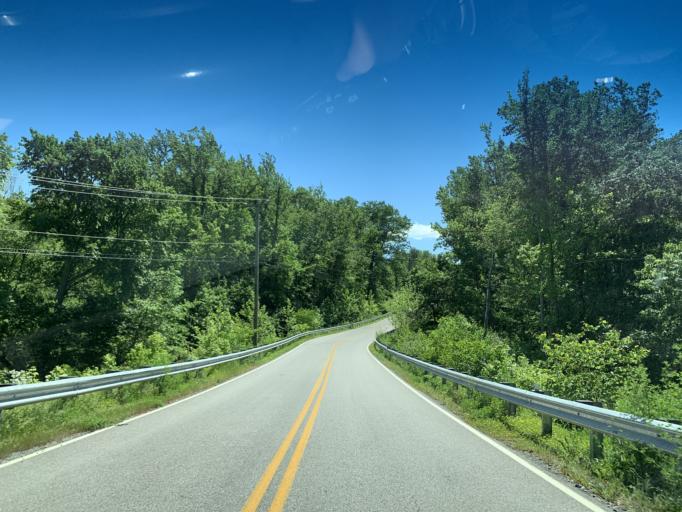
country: US
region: Maryland
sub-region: Cecil County
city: Charlestown
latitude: 39.5206
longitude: -75.9421
